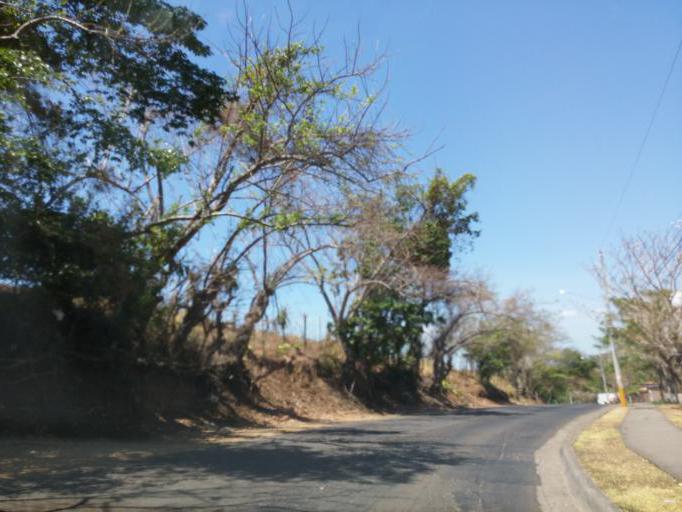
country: CR
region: Alajuela
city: Alajuela
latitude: 10.0165
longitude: -84.2263
